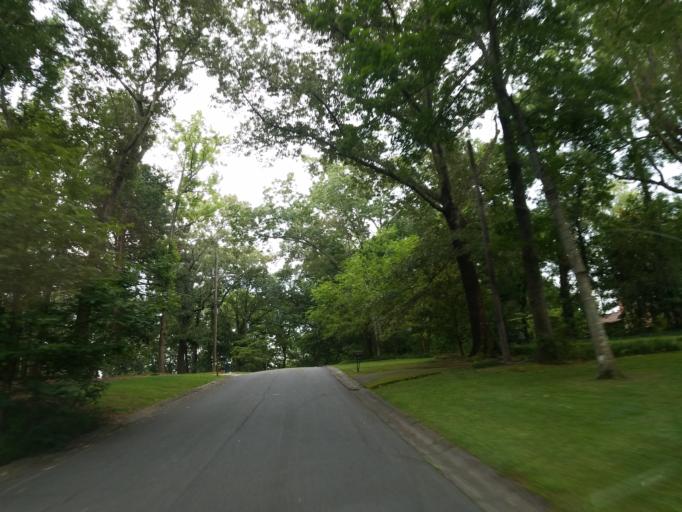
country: US
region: Georgia
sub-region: Cobb County
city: Marietta
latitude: 33.9391
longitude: -84.5509
